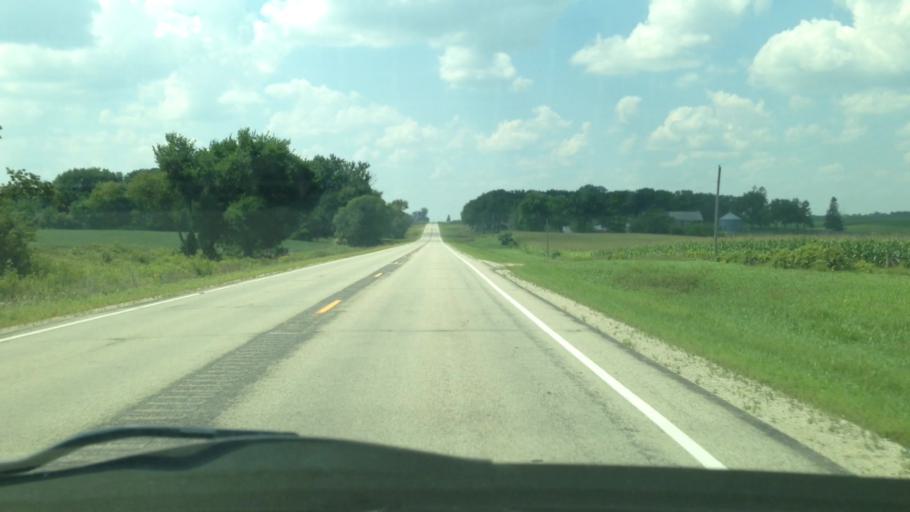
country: US
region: Minnesota
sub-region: Olmsted County
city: Stewartville
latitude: 43.8554
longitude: -92.4113
